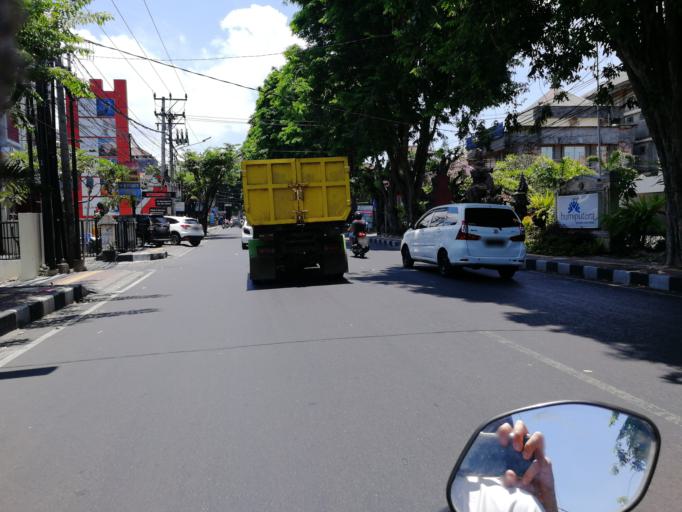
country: ID
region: Bali
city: Denpasar
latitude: -8.6688
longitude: 115.2154
